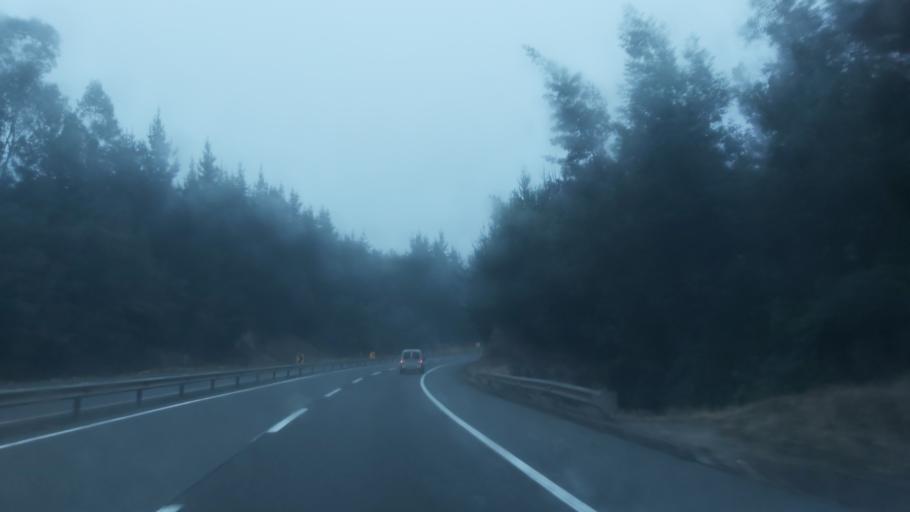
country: CL
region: Biobio
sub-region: Provincia de Concepcion
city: Penco
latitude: -36.7407
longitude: -72.9028
